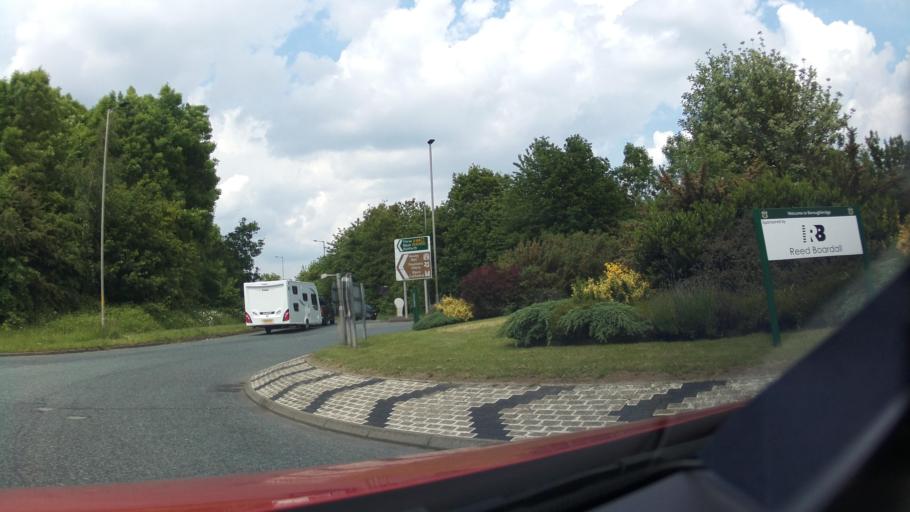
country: GB
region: England
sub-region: North Yorkshire
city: Boroughbridge
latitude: 54.0918
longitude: -1.4045
